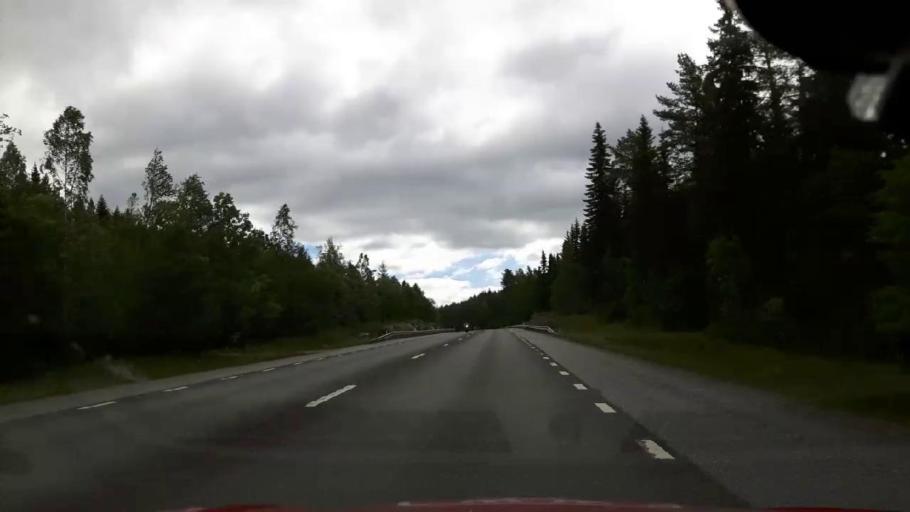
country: SE
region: Jaemtland
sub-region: Braecke Kommun
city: Braecke
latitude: 62.7031
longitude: 15.5056
